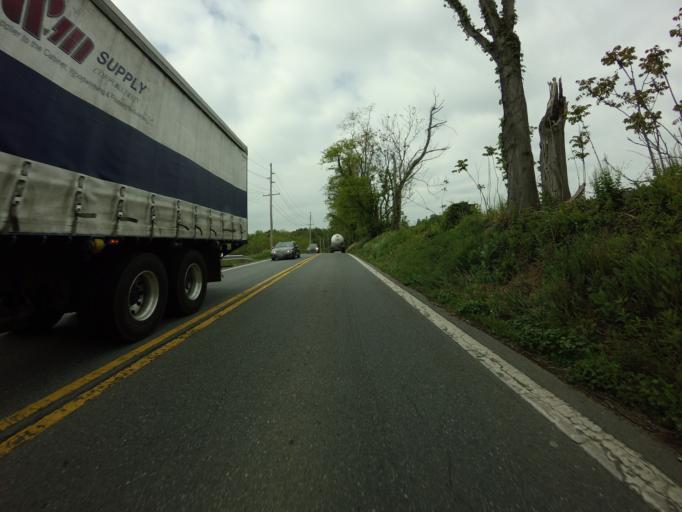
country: US
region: Maryland
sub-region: Frederick County
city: Green Valley
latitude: 39.2917
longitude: -77.3095
